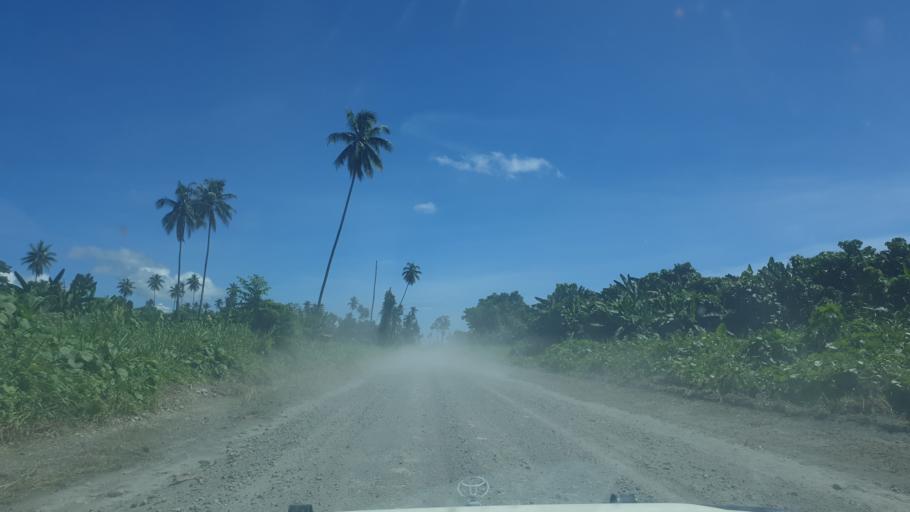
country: PG
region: Bougainville
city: Arawa
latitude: -5.9814
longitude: 155.3537
